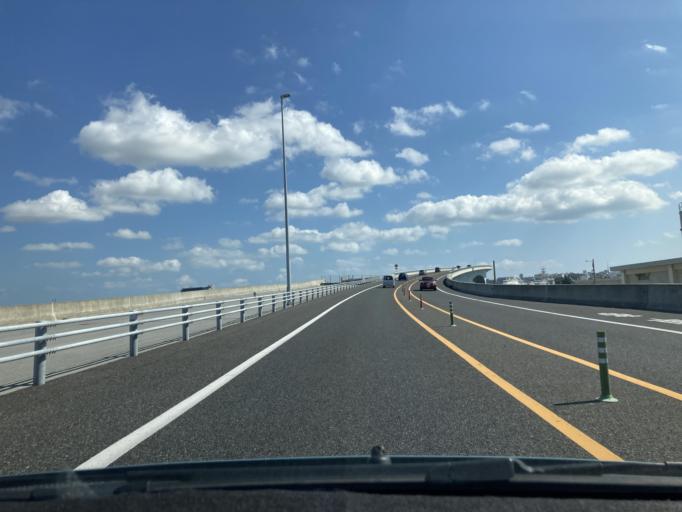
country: JP
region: Okinawa
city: Ginowan
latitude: 26.2735
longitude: 127.7181
